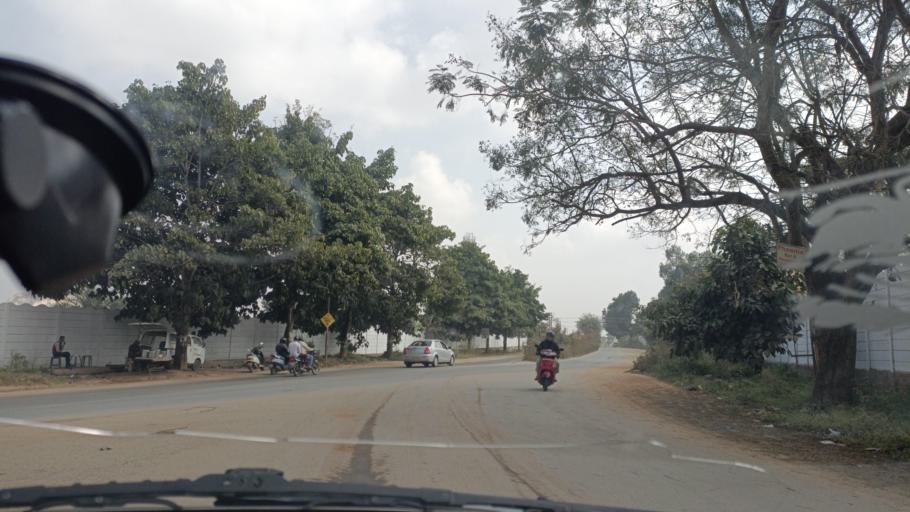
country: IN
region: Karnataka
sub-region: Bangalore Urban
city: Yelahanka
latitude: 13.1516
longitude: 77.6115
